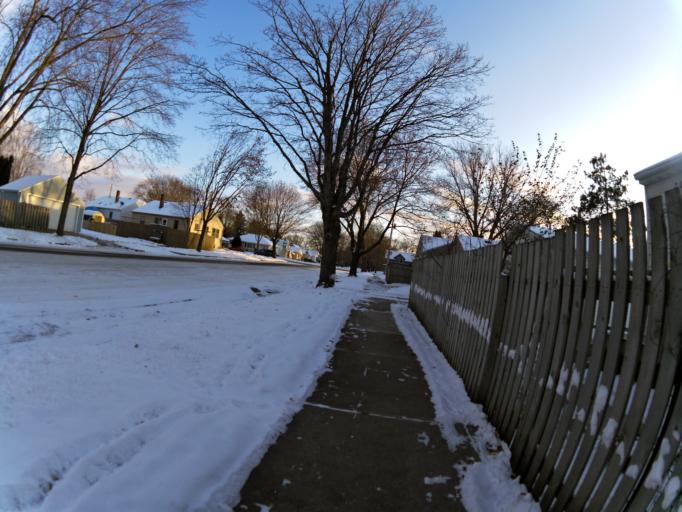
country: US
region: Minnesota
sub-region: Olmsted County
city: Rochester
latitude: 44.0367
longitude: -92.4541
